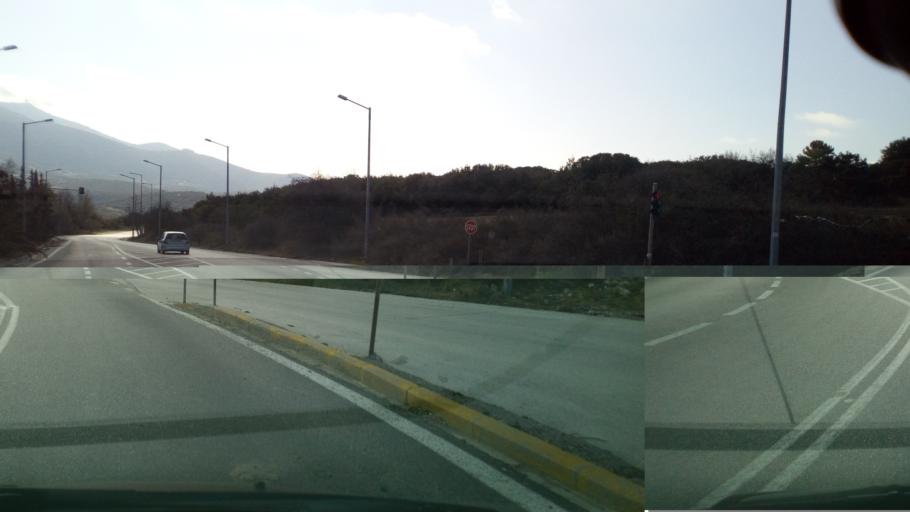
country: GR
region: Central Macedonia
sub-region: Nomos Thessalonikis
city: Chortiatis
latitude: 40.6239
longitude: 23.0627
